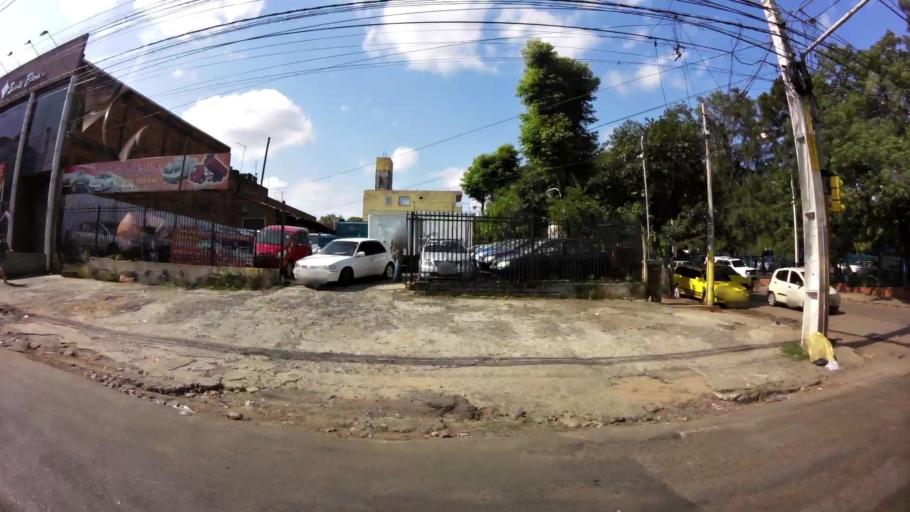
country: PY
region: Central
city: Fernando de la Mora
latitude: -25.3368
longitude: -57.5291
